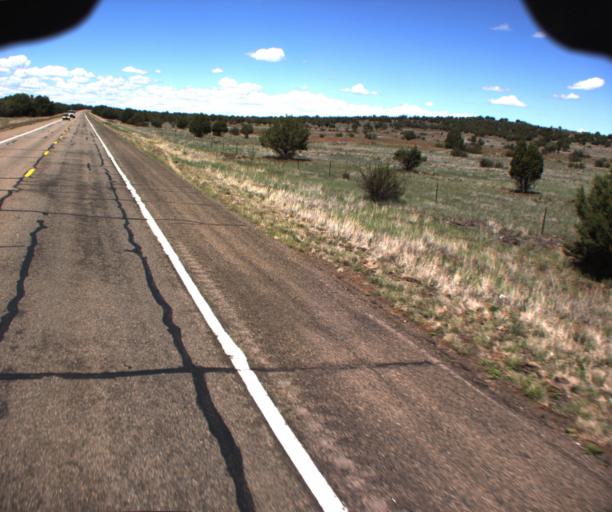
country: US
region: Arizona
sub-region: Yavapai County
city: Paulden
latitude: 35.1557
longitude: -112.4530
